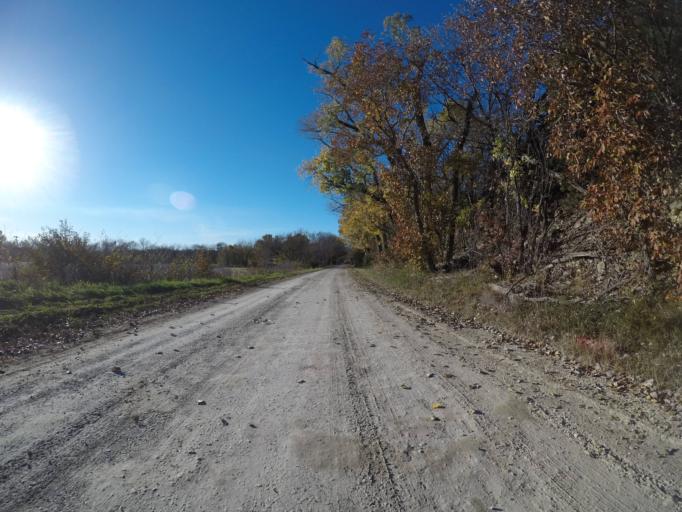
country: US
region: Kansas
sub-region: Riley County
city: Fort Riley North
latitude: 39.2636
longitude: -96.7790
